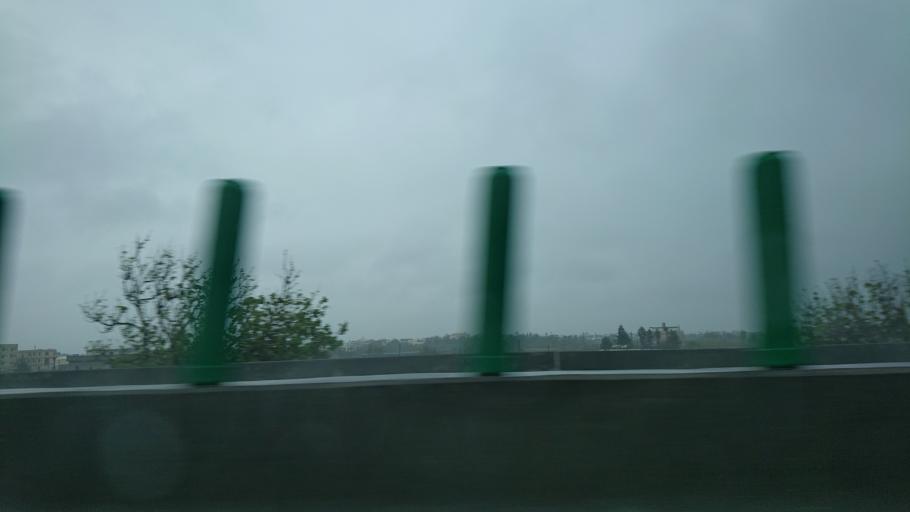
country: TW
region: Taiwan
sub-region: Chiayi
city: Taibao
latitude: 23.7125
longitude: 120.1978
